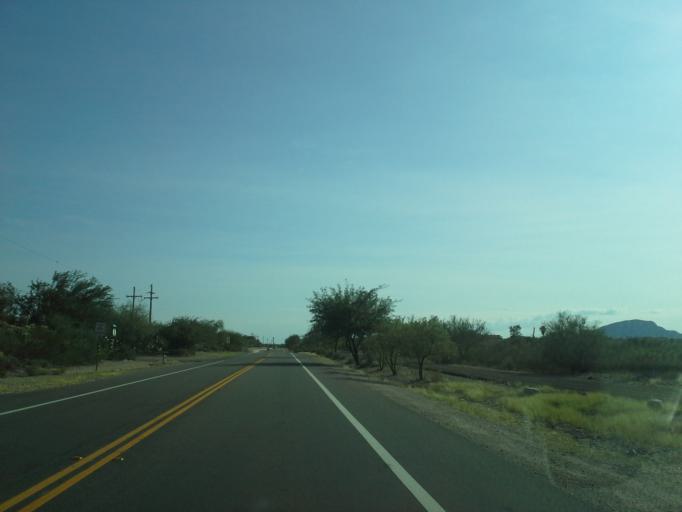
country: US
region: Arizona
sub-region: Pima County
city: Flowing Wells
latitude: 32.2462
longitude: -111.0205
